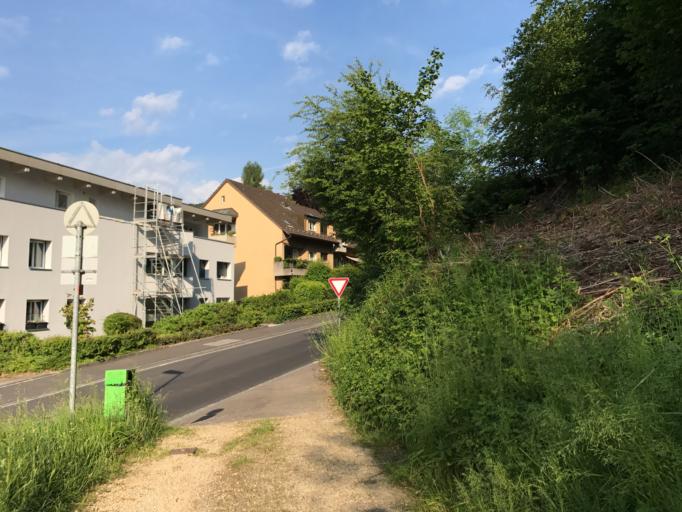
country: CH
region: Basel-City
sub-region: Basel-Stadt
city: Bettingen
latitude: 47.5727
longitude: 7.6564
